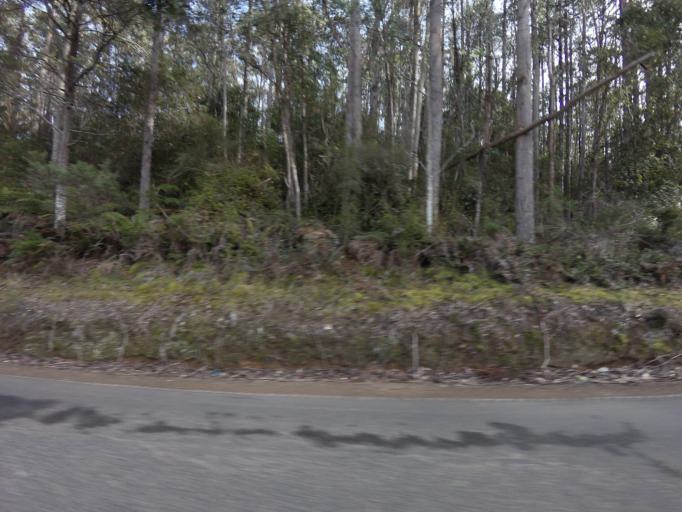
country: AU
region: Tasmania
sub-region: Kingborough
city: Margate
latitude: -43.0105
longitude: 147.1661
